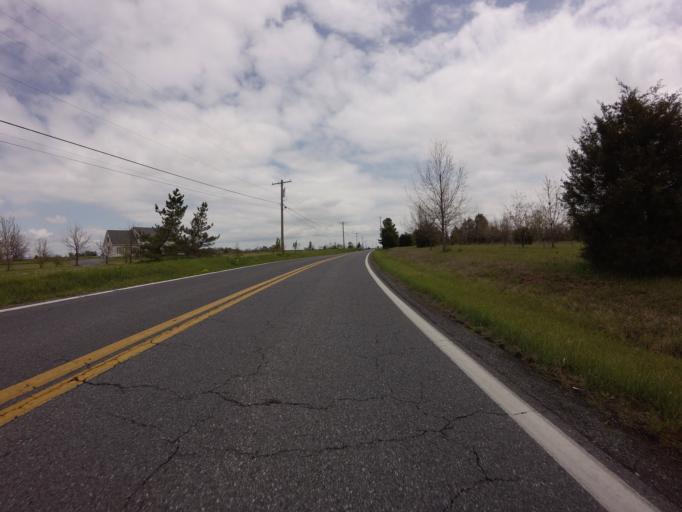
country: US
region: Maryland
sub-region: Frederick County
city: Woodsboro
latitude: 39.5705
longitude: -77.3687
